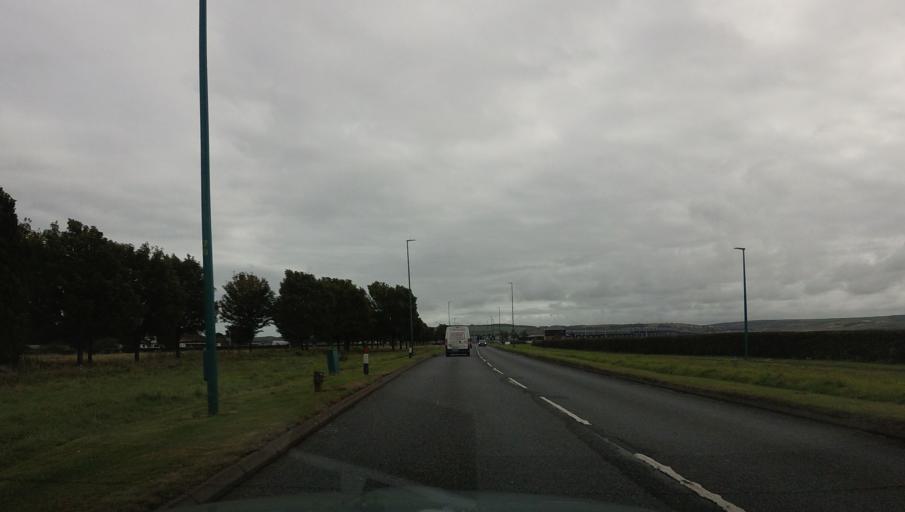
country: GB
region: Scotland
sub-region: Dundee City
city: Dundee
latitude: 56.4534
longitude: -3.0002
